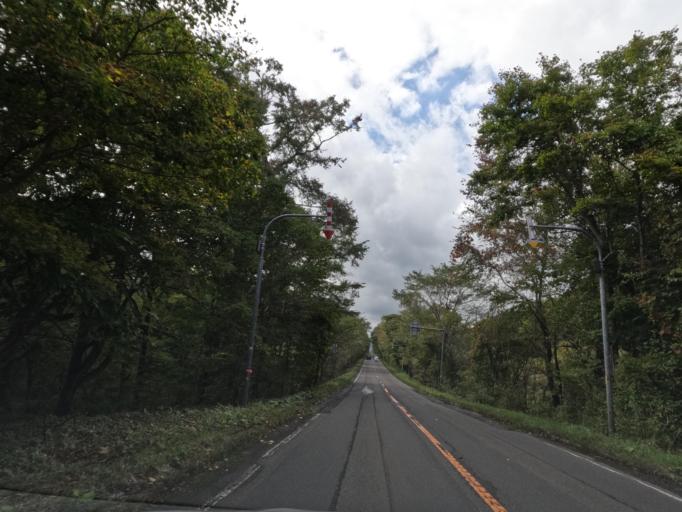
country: JP
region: Hokkaido
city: Chitose
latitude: 42.7917
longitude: 141.5235
